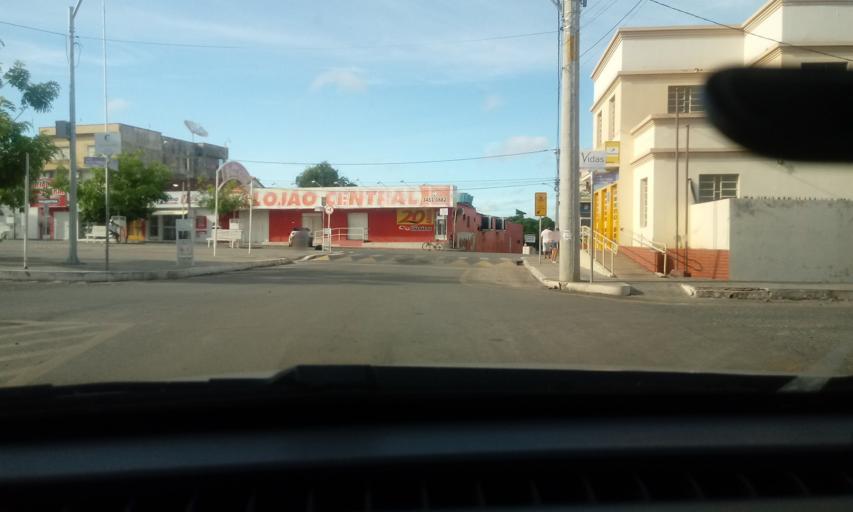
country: BR
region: Bahia
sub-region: Guanambi
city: Guanambi
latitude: -14.2276
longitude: -42.7812
